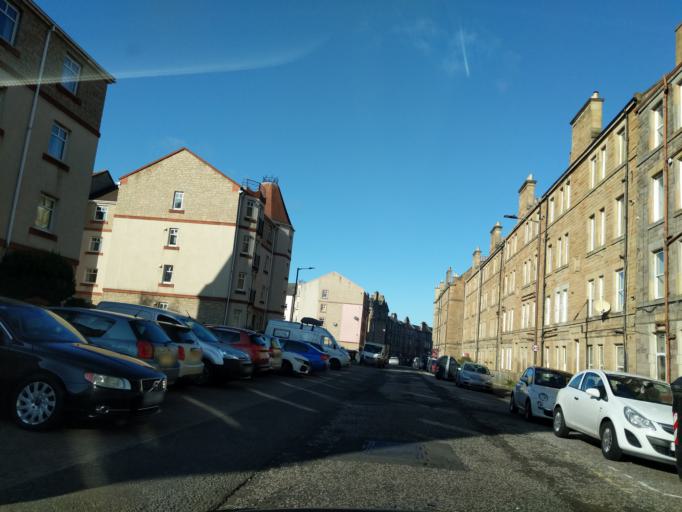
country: GB
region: Scotland
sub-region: Edinburgh
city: Colinton
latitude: 55.9362
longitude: -3.2340
